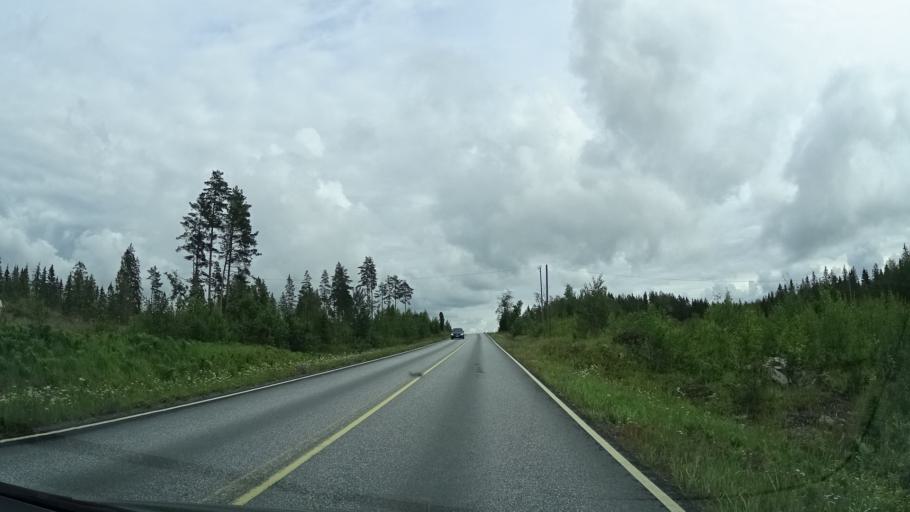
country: FI
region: Haeme
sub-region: Forssa
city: Humppila
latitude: 61.0965
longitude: 23.3525
